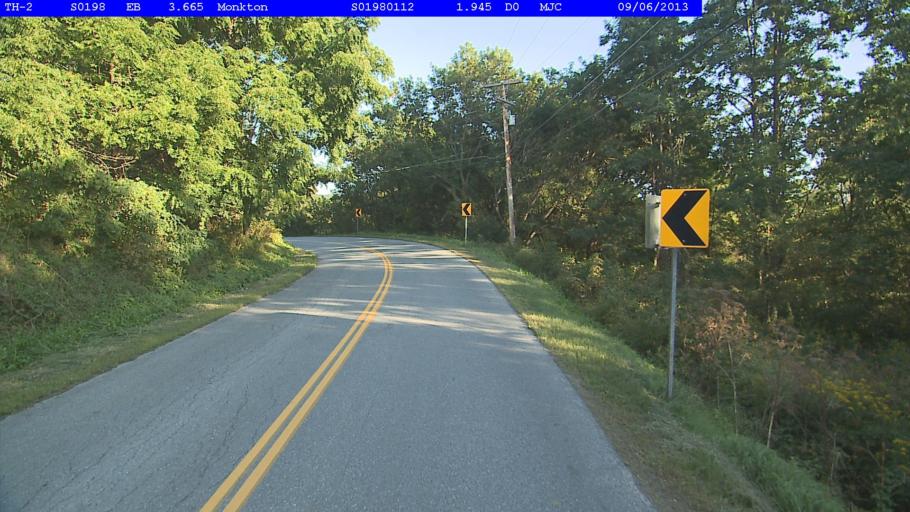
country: US
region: Vermont
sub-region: Chittenden County
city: Hinesburg
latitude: 44.2431
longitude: -73.1630
